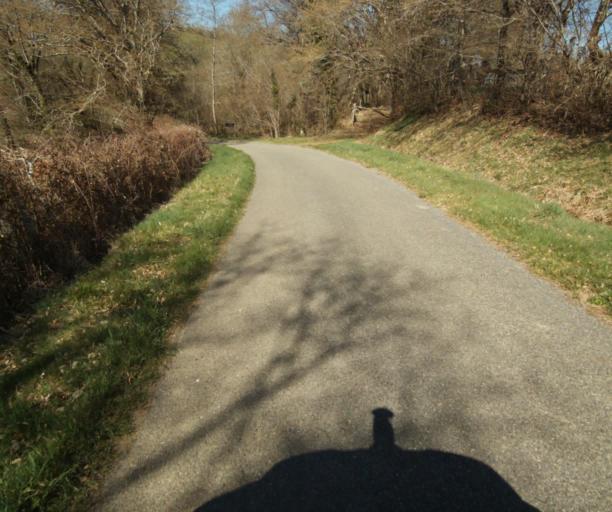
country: FR
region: Limousin
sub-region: Departement de la Correze
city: Chamboulive
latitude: 45.4582
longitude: 1.6773
